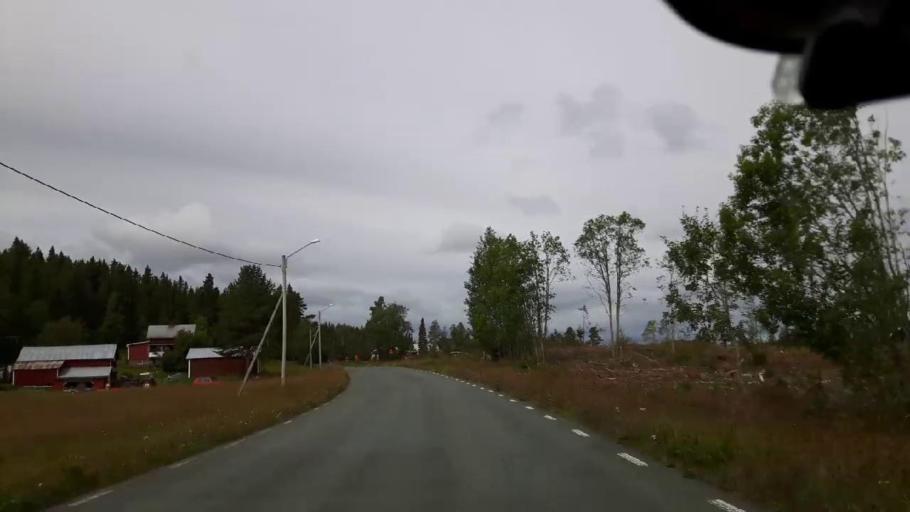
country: SE
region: Jaemtland
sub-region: Krokoms Kommun
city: Valla
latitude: 63.4619
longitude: 14.0299
